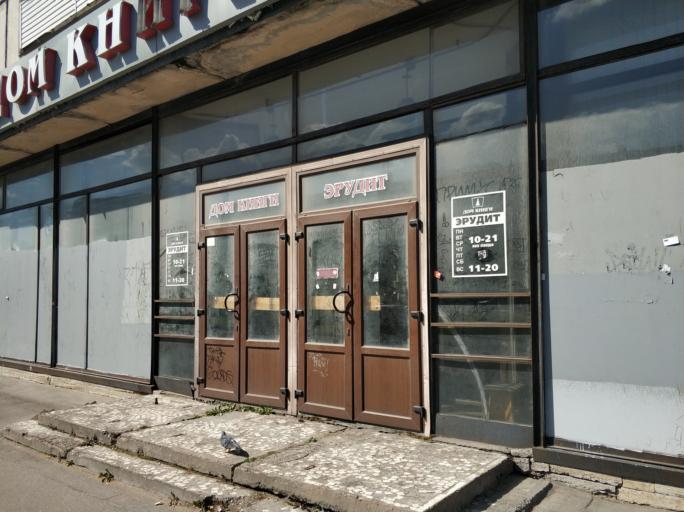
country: RU
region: Leningrad
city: Akademicheskoe
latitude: 60.0201
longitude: 30.4040
